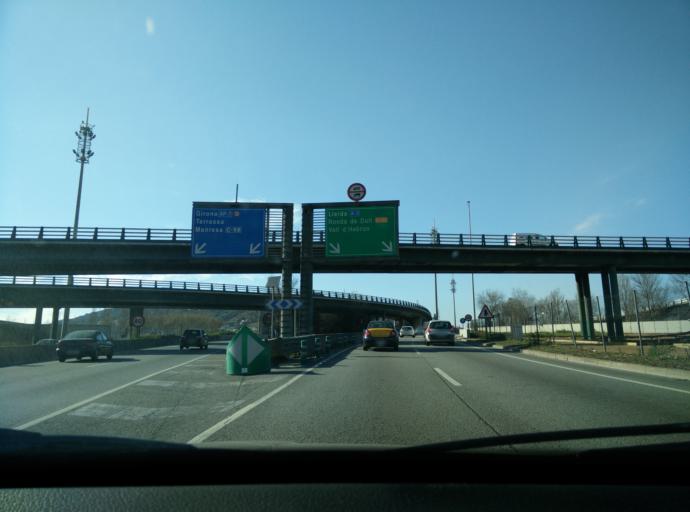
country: ES
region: Catalonia
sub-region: Provincia de Barcelona
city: Santa Coloma de Gramenet
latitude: 41.4493
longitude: 2.1990
